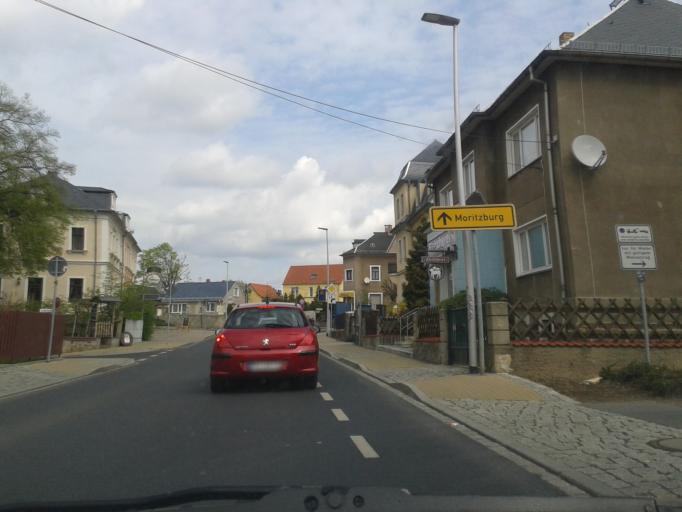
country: DE
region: Saxony
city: Radebeul
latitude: 51.1225
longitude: 13.6318
